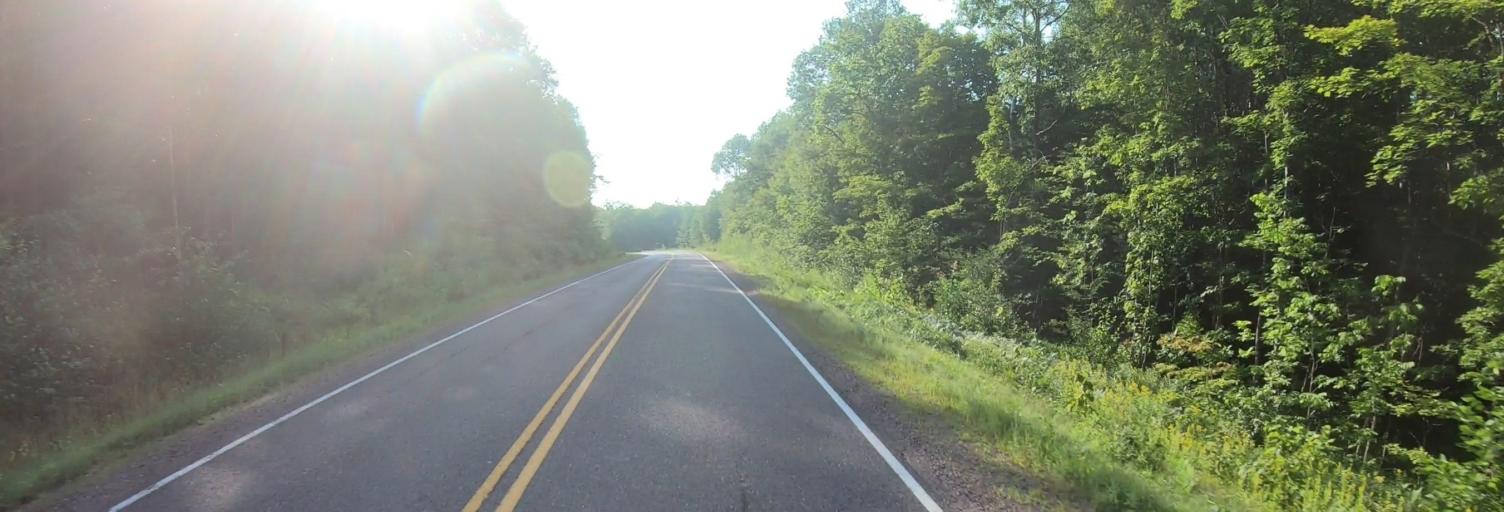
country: US
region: Wisconsin
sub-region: Ashland County
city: Ashland
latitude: 46.2940
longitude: -90.8099
